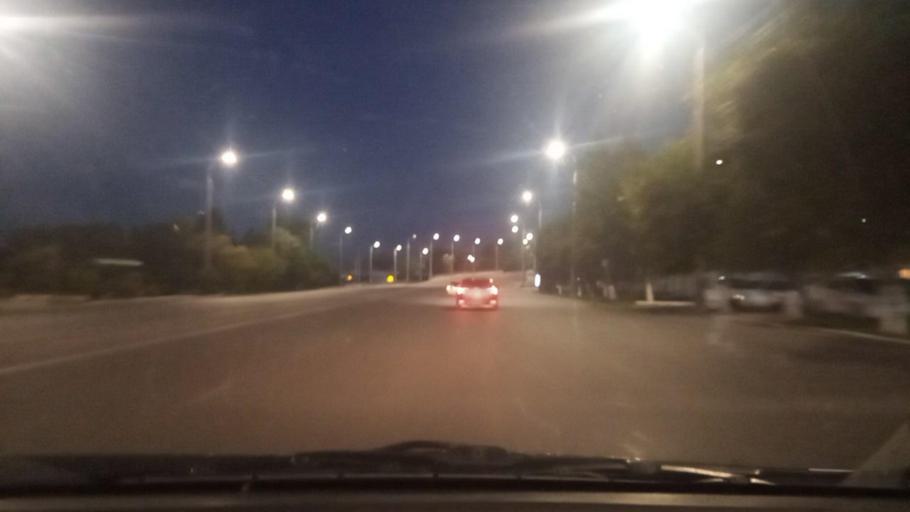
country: UZ
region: Toshkent Shahri
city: Tashkent
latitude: 41.2621
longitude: 69.2314
